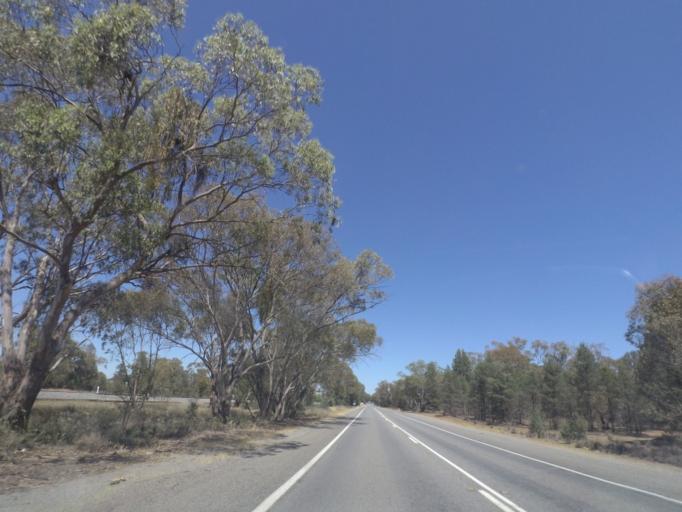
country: AU
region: New South Wales
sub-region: Narrandera
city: Narrandera
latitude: -34.7382
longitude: 146.5795
